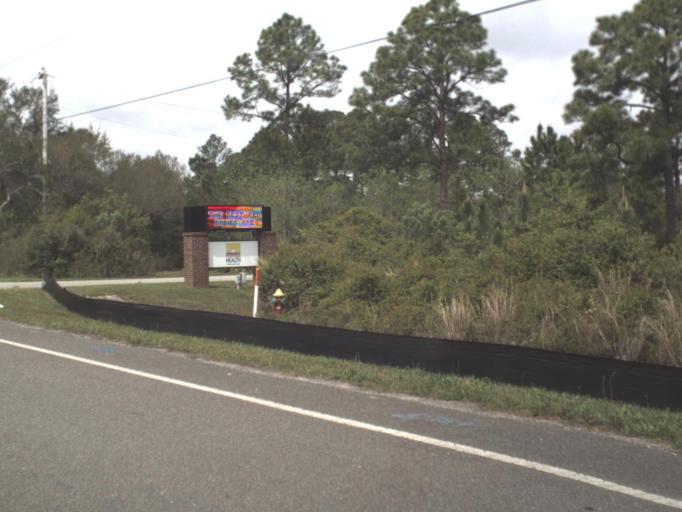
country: US
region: Florida
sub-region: Santa Rosa County
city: Woodlawn Beach
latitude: 30.4029
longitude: -86.9794
